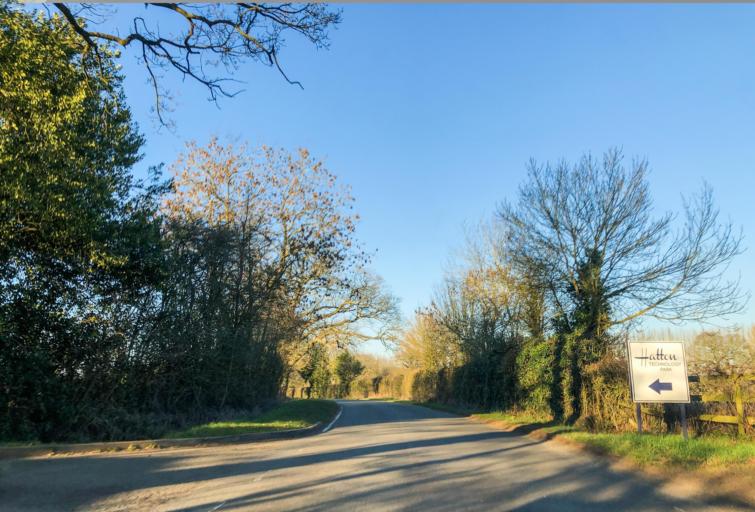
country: GB
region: England
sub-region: Warwickshire
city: Wroxall
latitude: 52.2891
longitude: -1.6609
